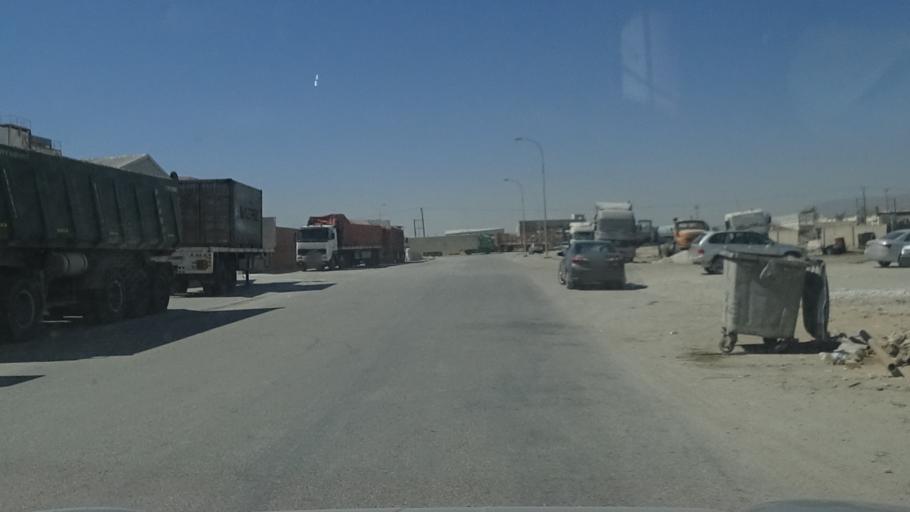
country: OM
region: Zufar
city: Salalah
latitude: 17.0325
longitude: 54.0463
